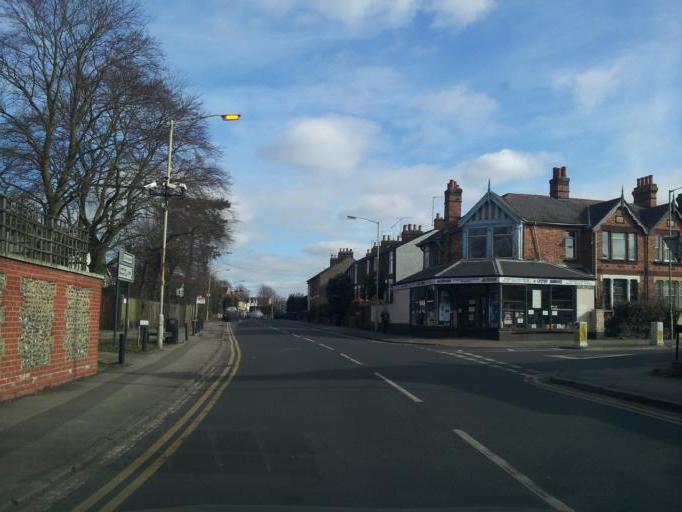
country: GB
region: England
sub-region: Hertfordshire
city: St Albans
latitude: 51.7585
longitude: -0.3320
